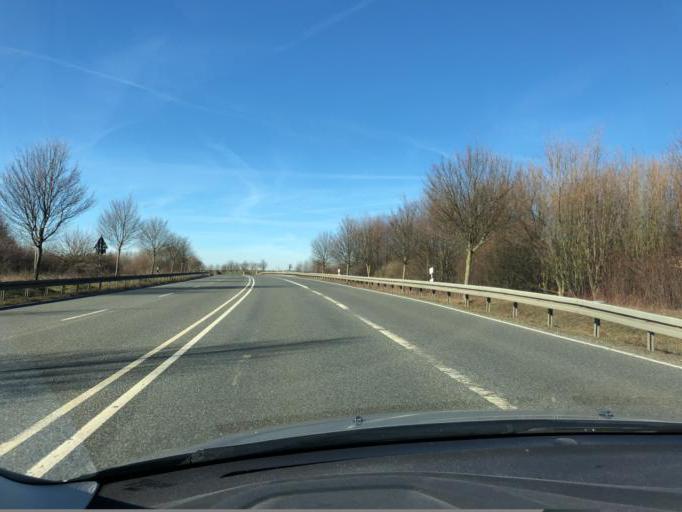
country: DE
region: Lower Saxony
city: Langelsheim
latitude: 51.9461
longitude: 10.3087
